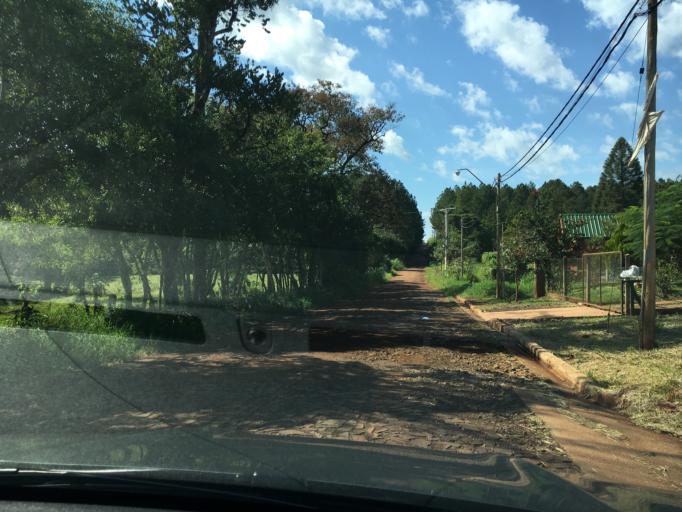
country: AR
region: Misiones
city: Puerto Rico
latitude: -26.8161
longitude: -55.0163
